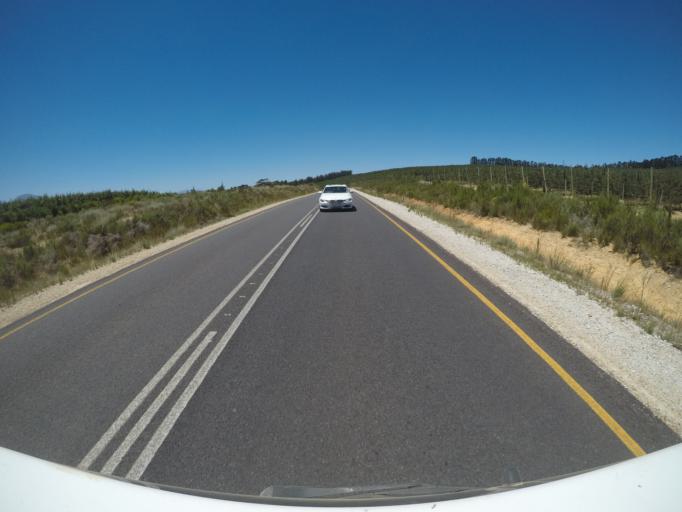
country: ZA
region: Western Cape
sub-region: Overberg District Municipality
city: Grabouw
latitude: -34.0677
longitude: 19.1213
